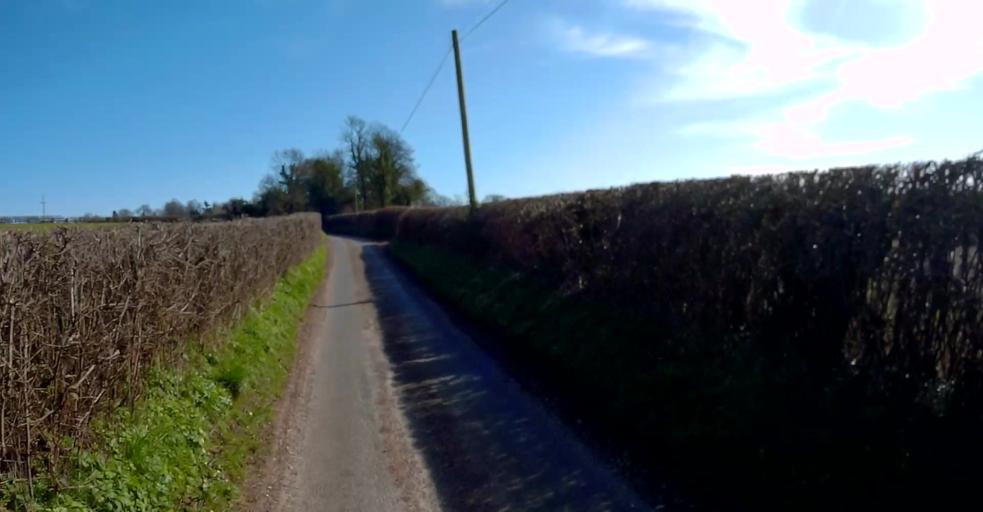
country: GB
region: England
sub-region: Hampshire
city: Four Marks
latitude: 51.1622
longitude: -1.0563
